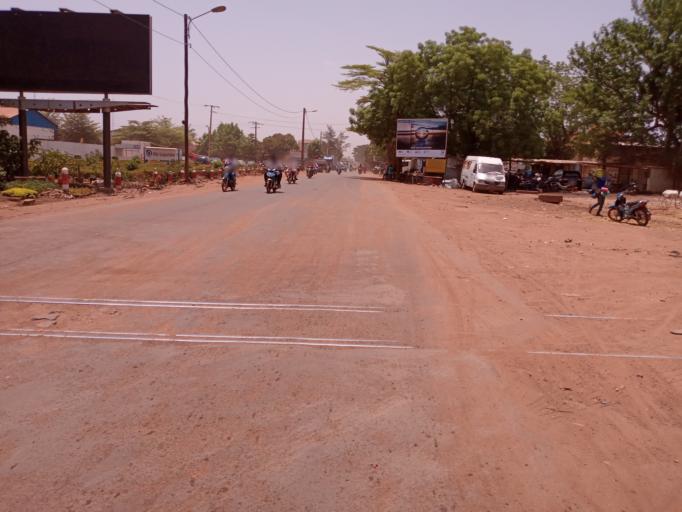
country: ML
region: Bamako
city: Bamako
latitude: 12.6482
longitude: -7.9735
